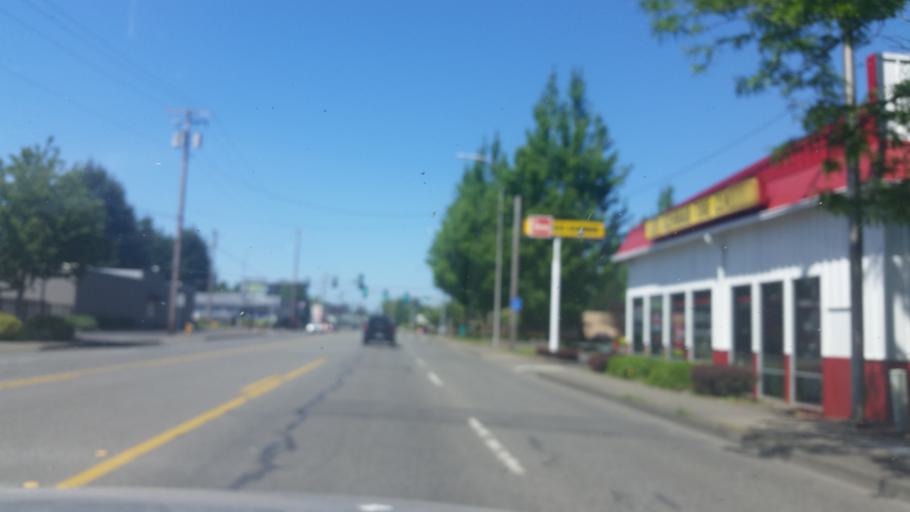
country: US
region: Washington
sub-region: Thurston County
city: Tumwater
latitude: 46.9964
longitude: -122.9075
